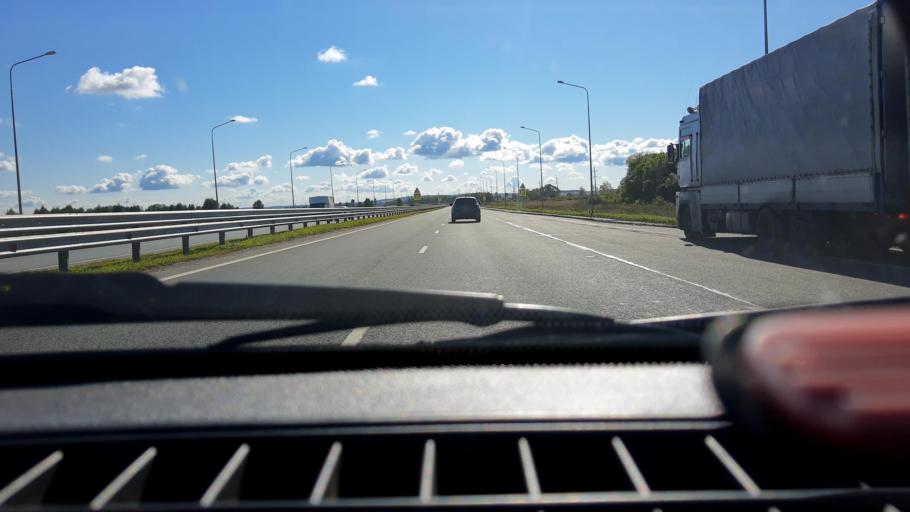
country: RU
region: Bashkortostan
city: Asanovo
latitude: 54.9171
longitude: 55.5873
